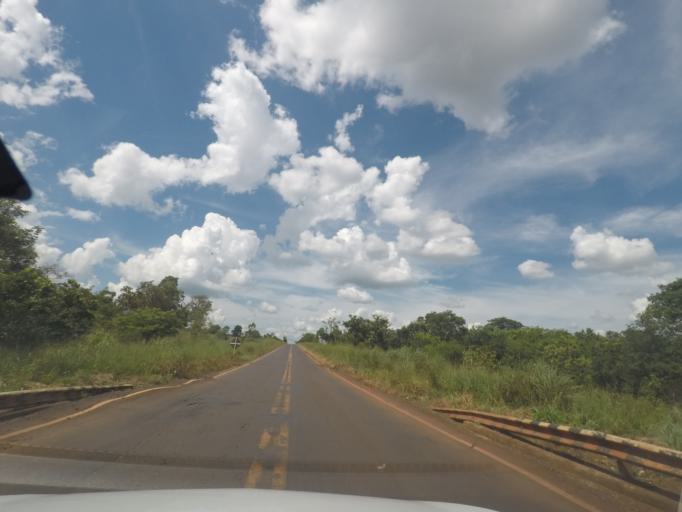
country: BR
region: Minas Gerais
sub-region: Conceicao Das Alagoas
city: Conceicao das Alagoas
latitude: -19.8166
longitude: -48.5889
